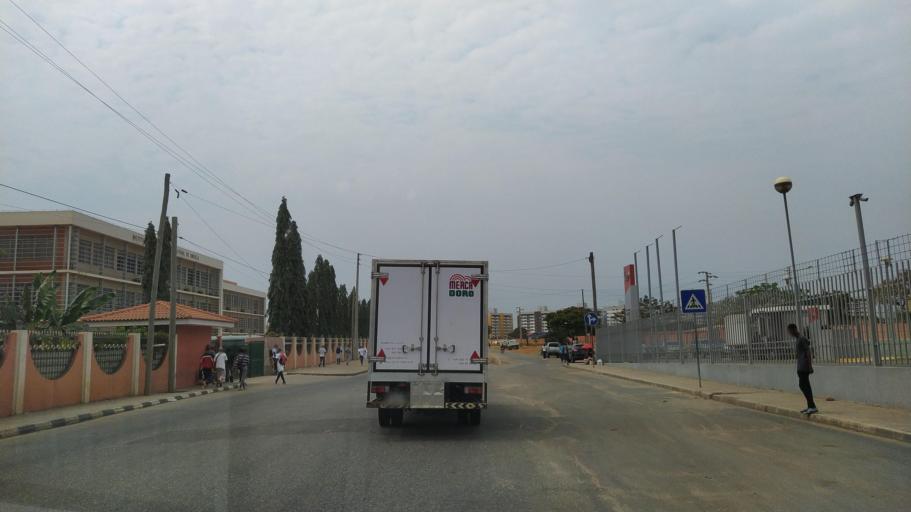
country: AO
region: Luanda
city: Luanda
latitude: -8.8568
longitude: 13.2890
